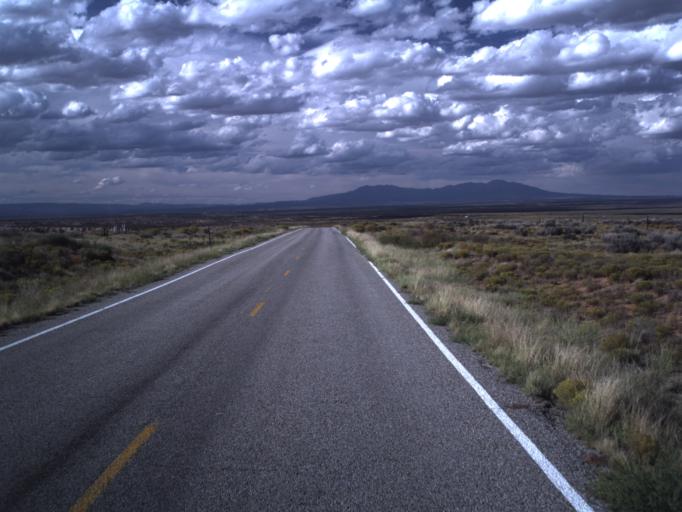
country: US
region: Utah
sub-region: San Juan County
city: Blanding
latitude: 37.3310
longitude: -109.3455
